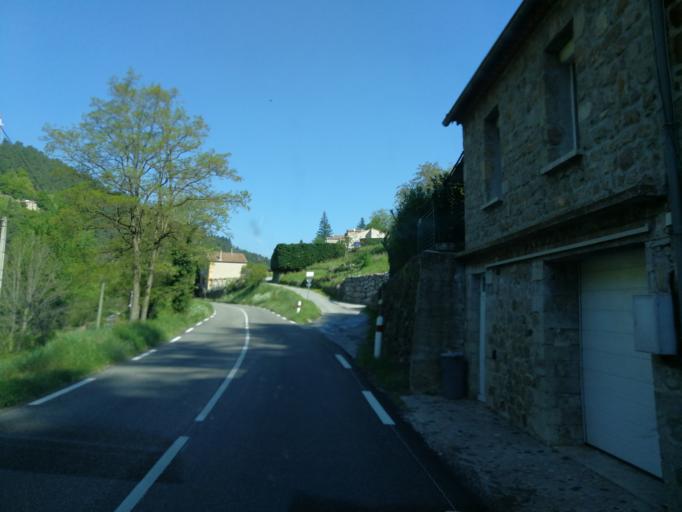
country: FR
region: Rhone-Alpes
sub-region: Departement de l'Ardeche
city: Saint-Sauveur-de-Montagut
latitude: 44.8416
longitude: 4.5750
